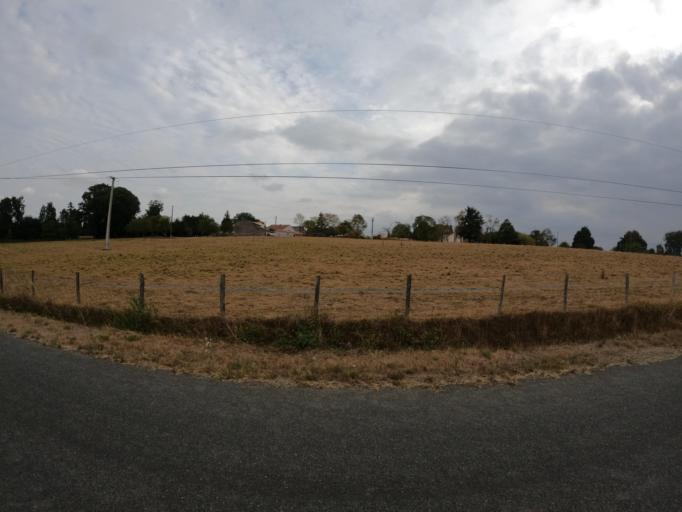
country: FR
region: Pays de la Loire
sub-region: Departement de Maine-et-Loire
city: La Romagne
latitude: 47.0552
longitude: -1.0117
